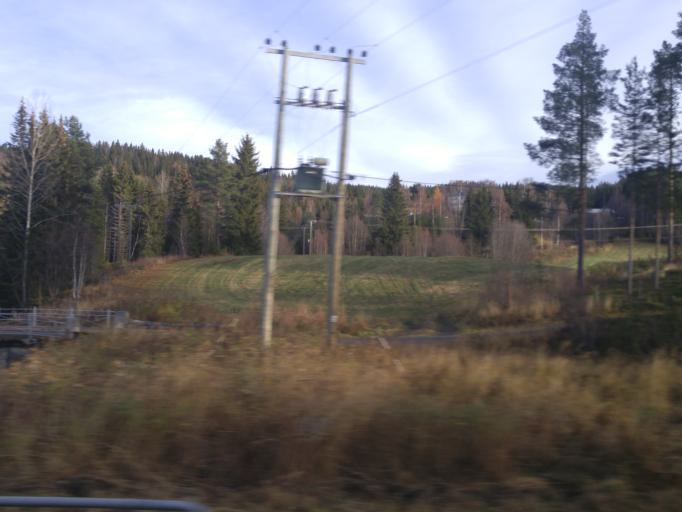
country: NO
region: Oppland
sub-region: Nord-Aurdal
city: Fagernes
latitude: 61.0593
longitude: 9.1646
